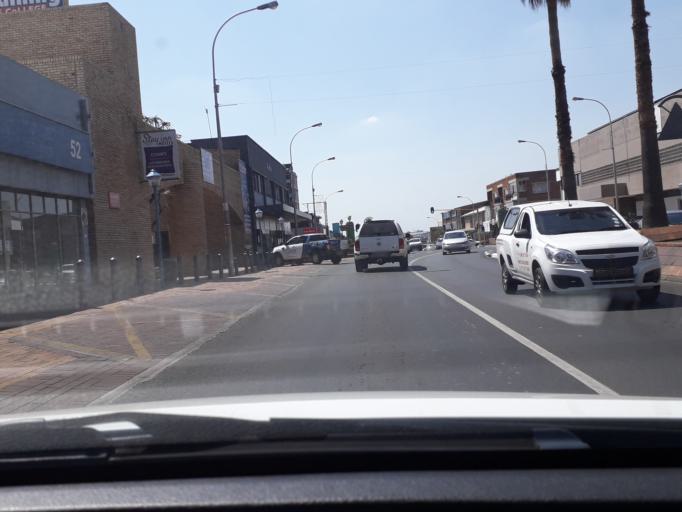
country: ZA
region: Gauteng
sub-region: City of Johannesburg Metropolitan Municipality
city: Modderfontein
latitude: -26.1441
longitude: 28.1544
